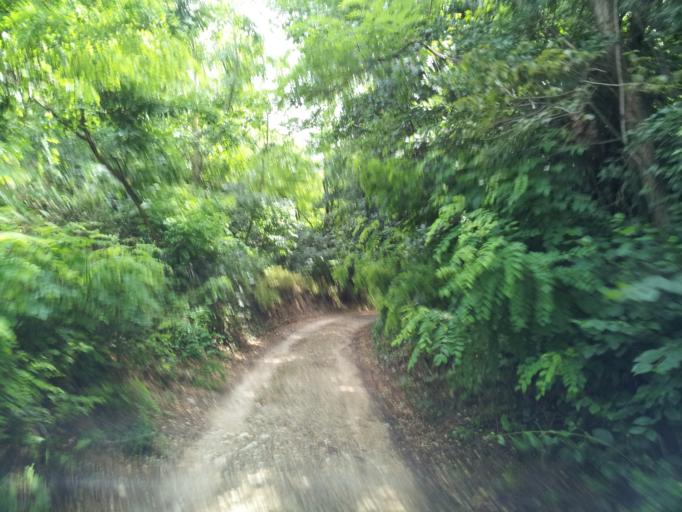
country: HU
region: Zala
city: Zalaszentgrot
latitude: 47.0062
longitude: 16.9758
